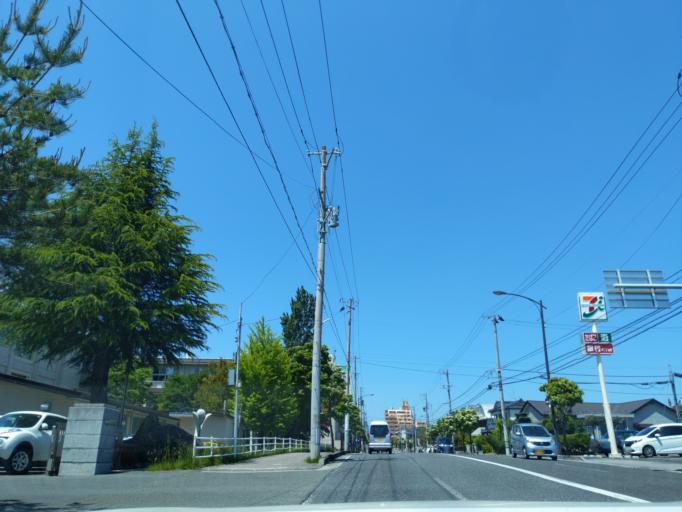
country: JP
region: Fukushima
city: Koriyama
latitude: 37.3866
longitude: 140.3697
